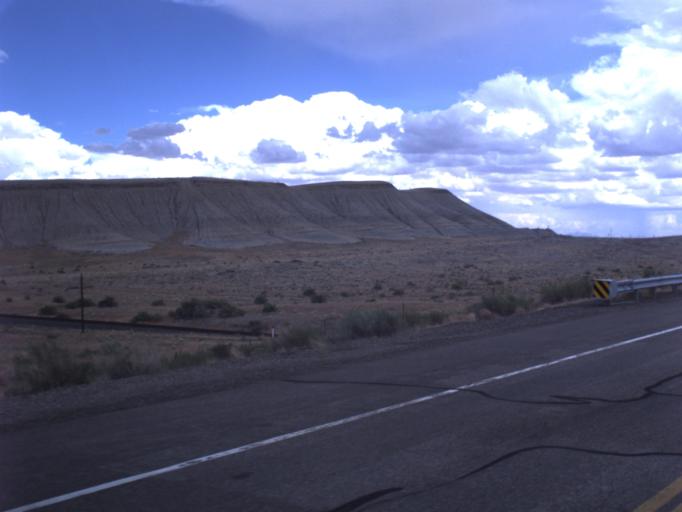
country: US
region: Utah
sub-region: Carbon County
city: East Carbon City
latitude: 38.9845
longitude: -110.1249
